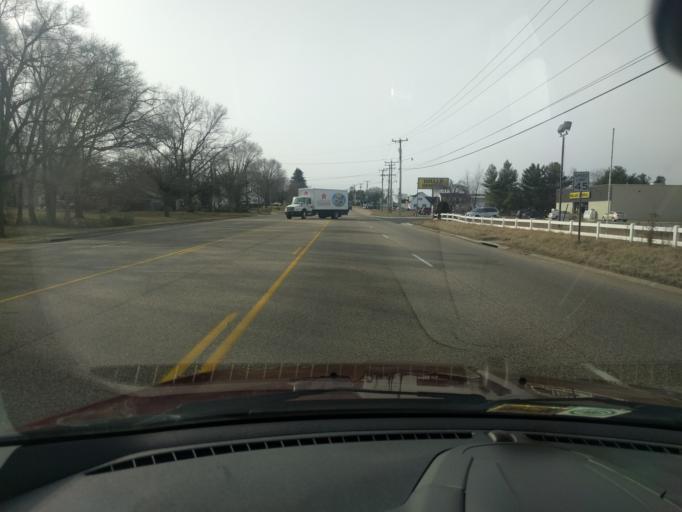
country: US
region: Virginia
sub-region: Augusta County
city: Stuarts Draft
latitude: 38.0370
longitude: -79.0280
